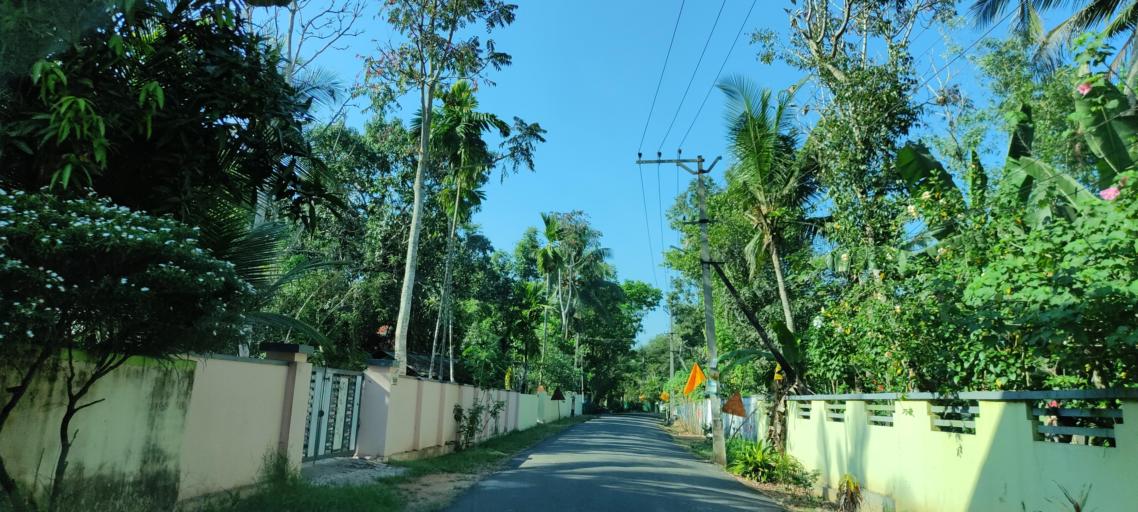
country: IN
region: Kerala
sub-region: Alappuzha
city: Shertallai
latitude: 9.6310
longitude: 76.3431
